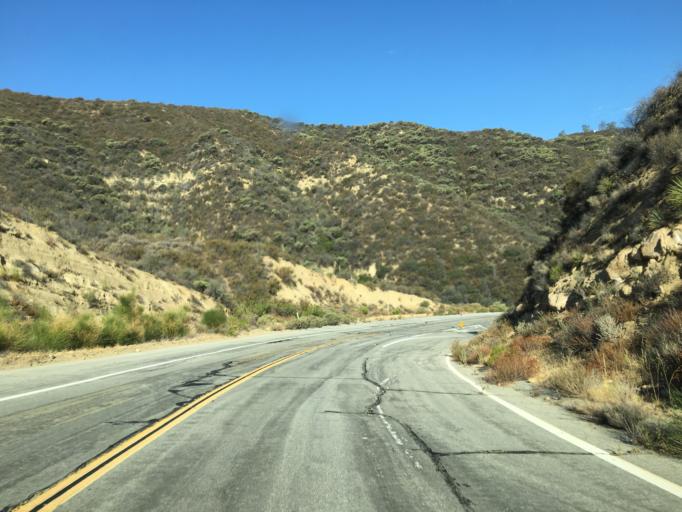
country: US
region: California
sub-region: Los Angeles County
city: Castaic
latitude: 34.5840
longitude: -118.6729
